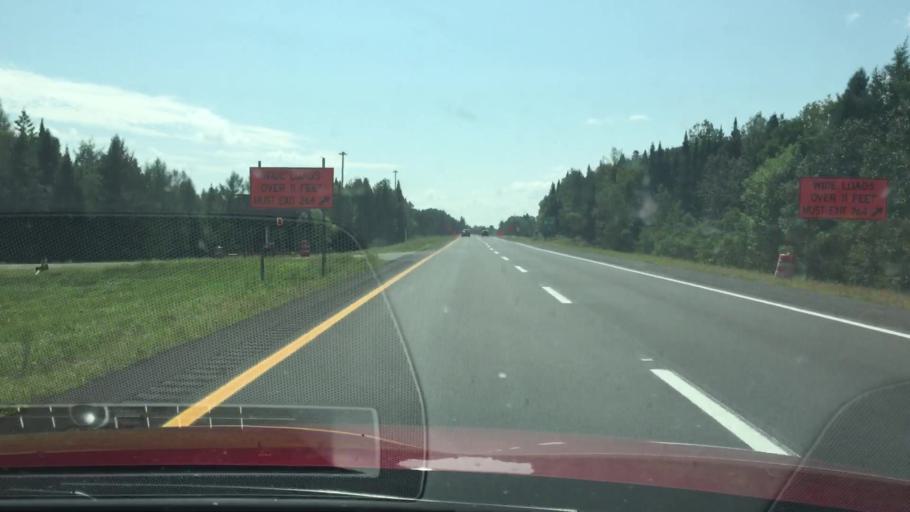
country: US
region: Maine
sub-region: Penobscot County
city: Patten
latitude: 45.8793
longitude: -68.4104
